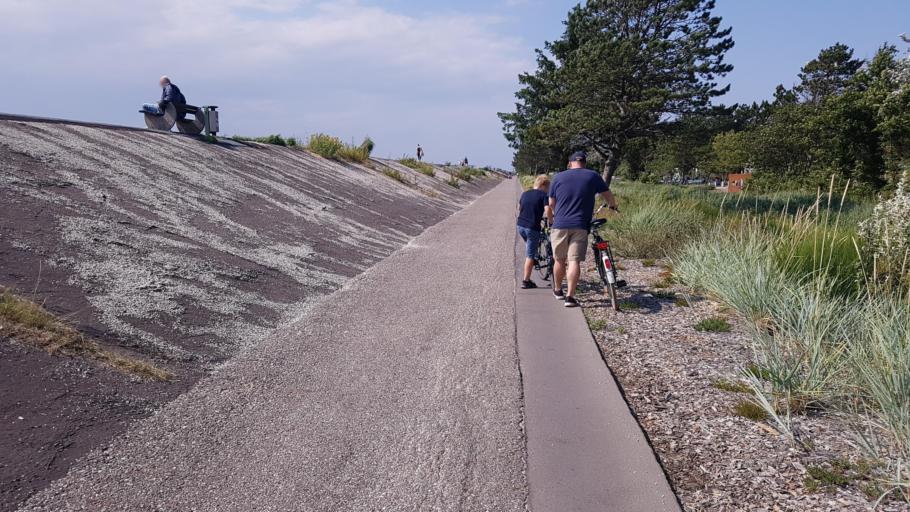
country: DE
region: Schleswig-Holstein
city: Sankt Peter-Ording
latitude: 54.3091
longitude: 8.6095
